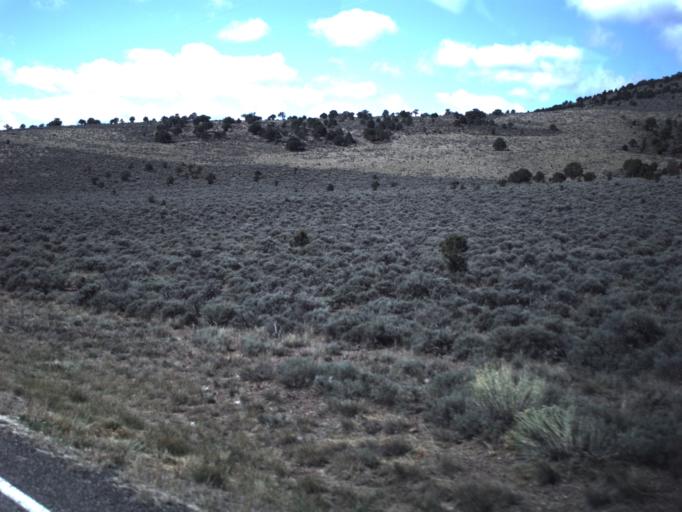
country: US
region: Utah
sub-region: Sevier County
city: Monroe
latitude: 38.5314
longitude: -111.8784
